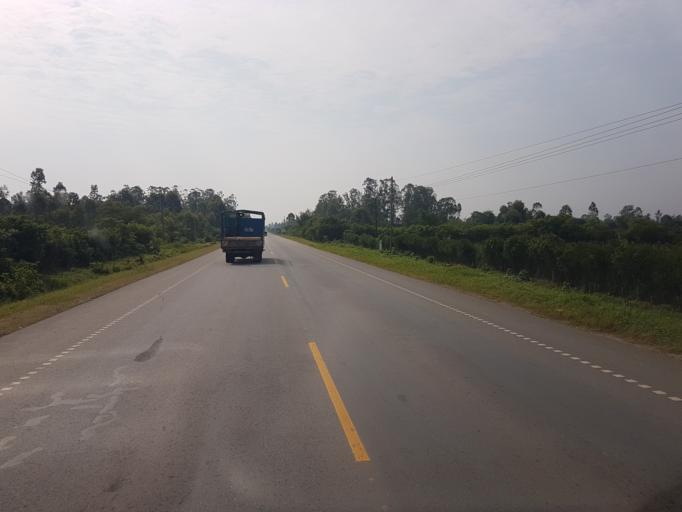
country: UG
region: Western Region
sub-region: Sheema District
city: Kibingo
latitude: -0.6350
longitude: 30.5248
